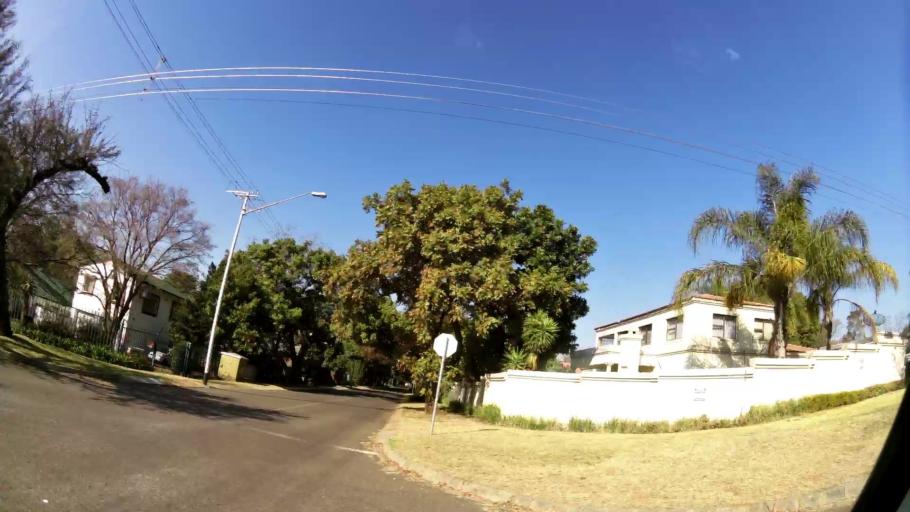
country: ZA
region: Gauteng
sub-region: City of Tshwane Metropolitan Municipality
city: Pretoria
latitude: -25.7861
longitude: 28.2629
